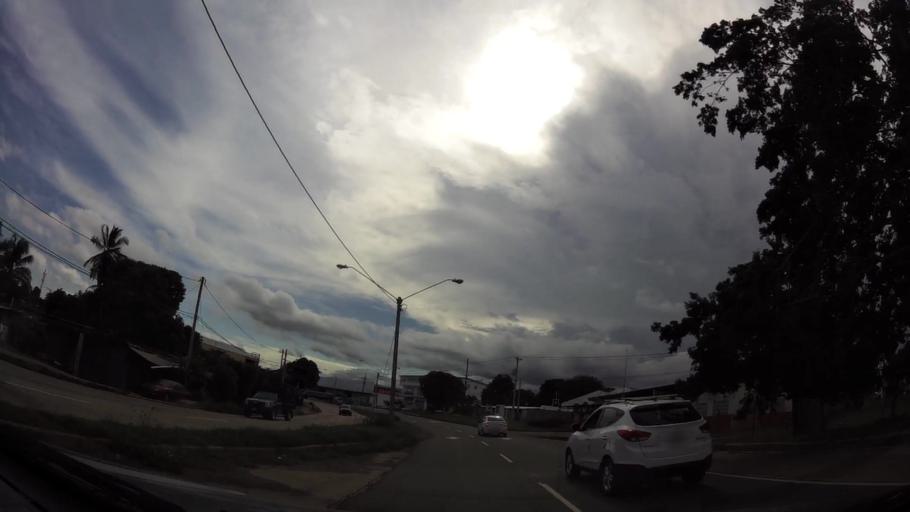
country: PA
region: Panama
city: Guadalupe
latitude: 8.8613
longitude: -79.8079
